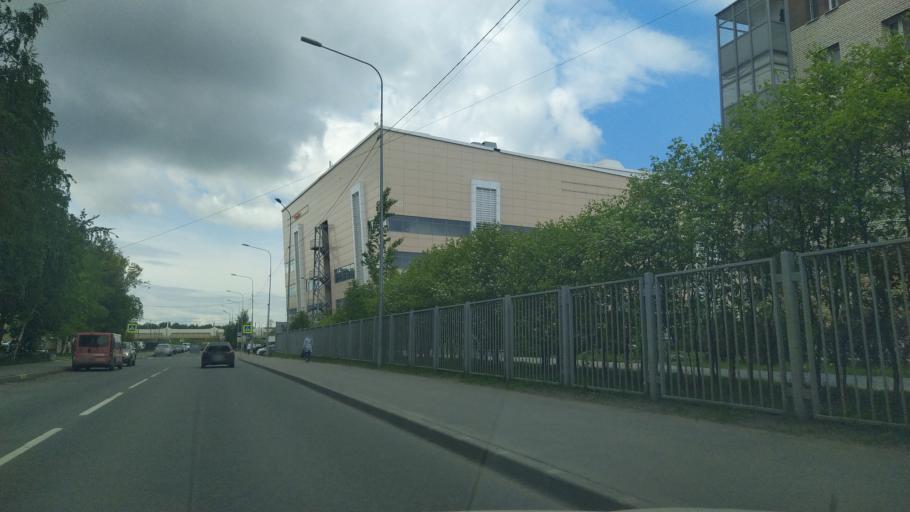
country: RU
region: Leningrad
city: Untolovo
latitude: 60.0221
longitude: 30.2281
